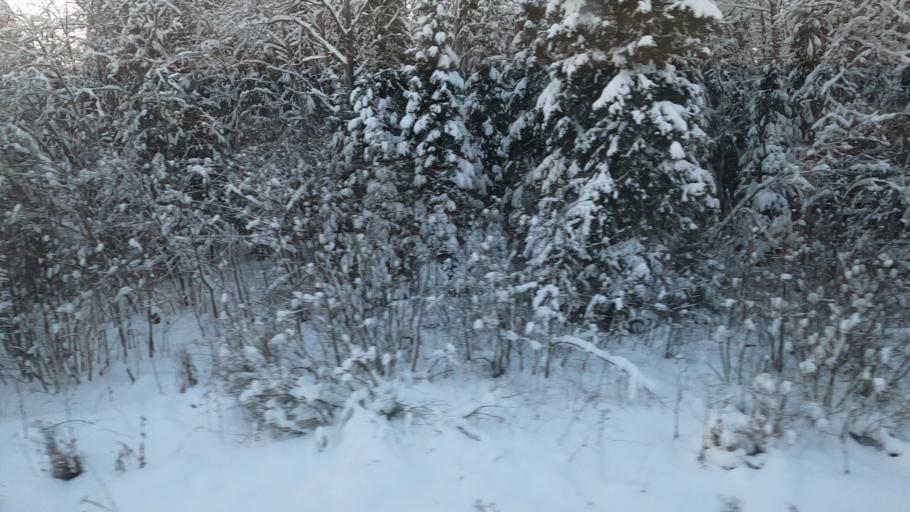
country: RU
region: Moskovskaya
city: Novo-Nikol'skoye
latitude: 56.5762
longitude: 37.5681
